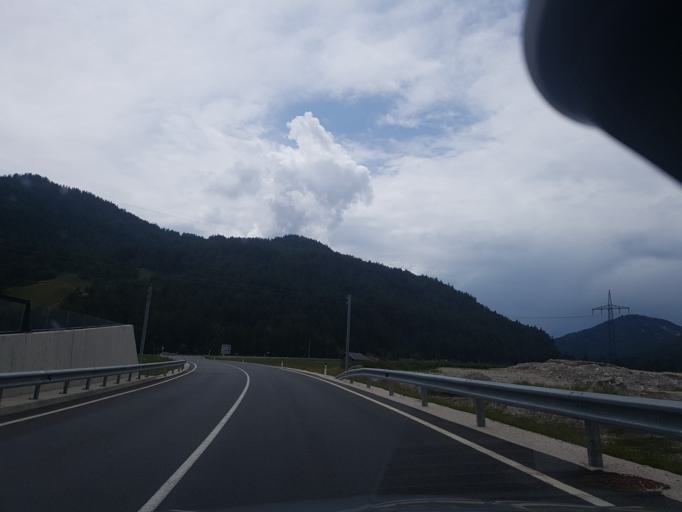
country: AT
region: Tyrol
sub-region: Politischer Bezirk Innsbruck Land
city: Scharnitz
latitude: 47.3879
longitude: 11.2524
